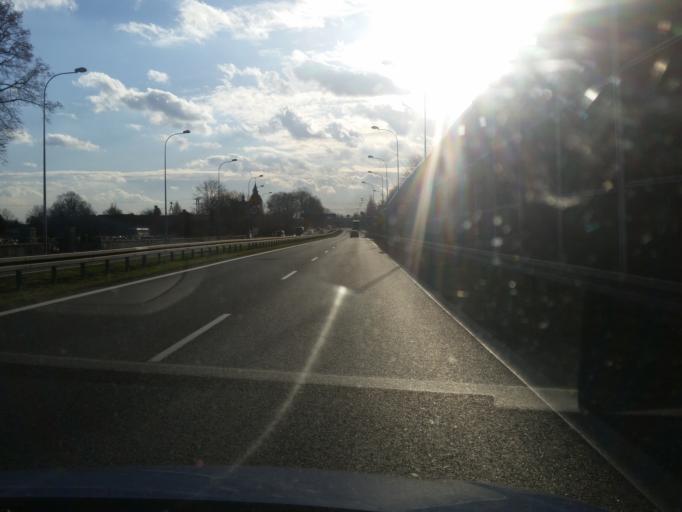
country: PL
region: Silesian Voivodeship
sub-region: Powiat bedzinski
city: Siewierz
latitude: 50.4148
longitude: 19.2062
